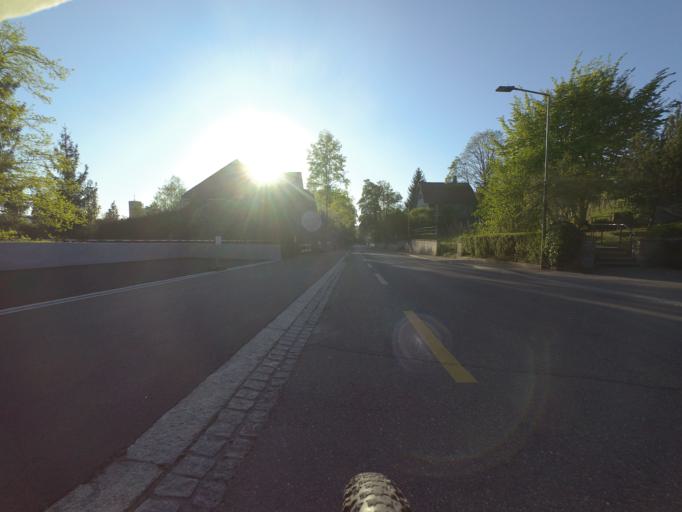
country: CH
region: Zurich
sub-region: Bezirk Winterthur
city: Stadt Winterthur (Kreis 1) / Lind
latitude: 47.5056
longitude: 8.7360
